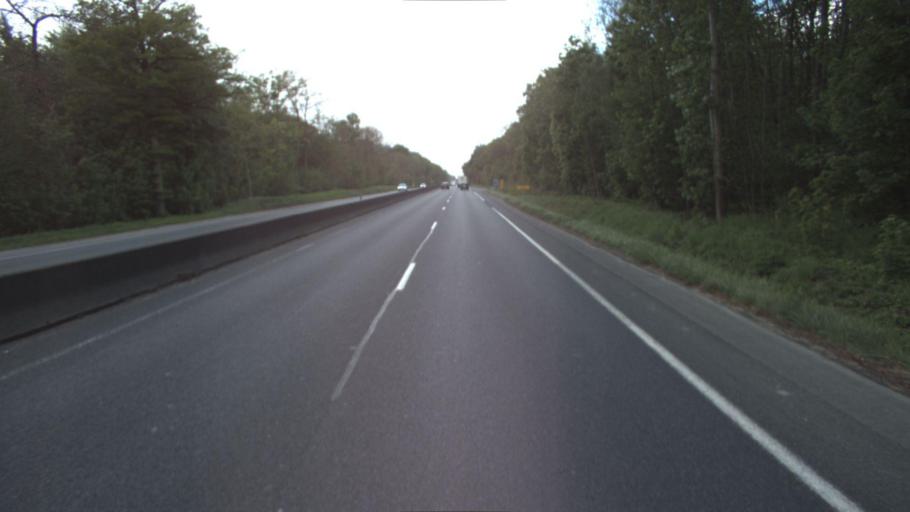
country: FR
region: Ile-de-France
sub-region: Departement de Seine-et-Marne
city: Roissy-en-Brie
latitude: 48.7706
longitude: 2.6308
